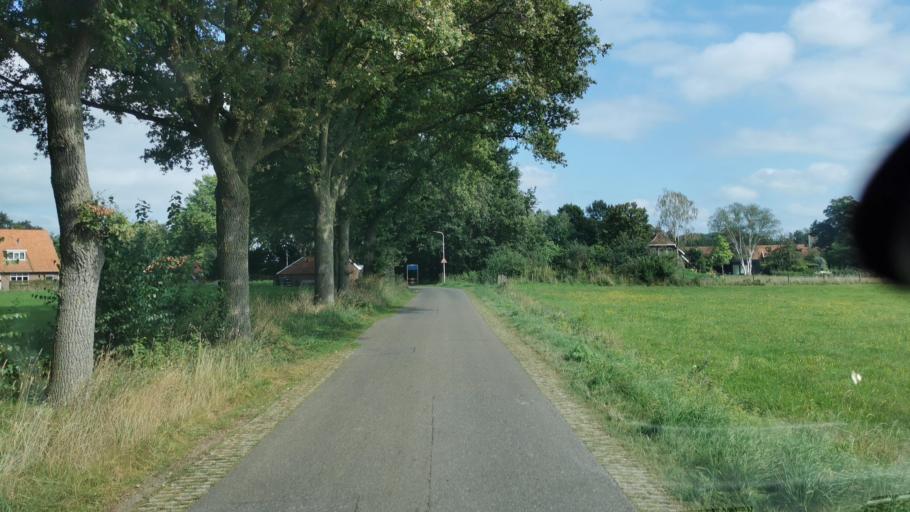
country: NL
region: Overijssel
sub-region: Gemeente Oldenzaal
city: Oldenzaal
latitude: 52.3455
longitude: 6.8492
